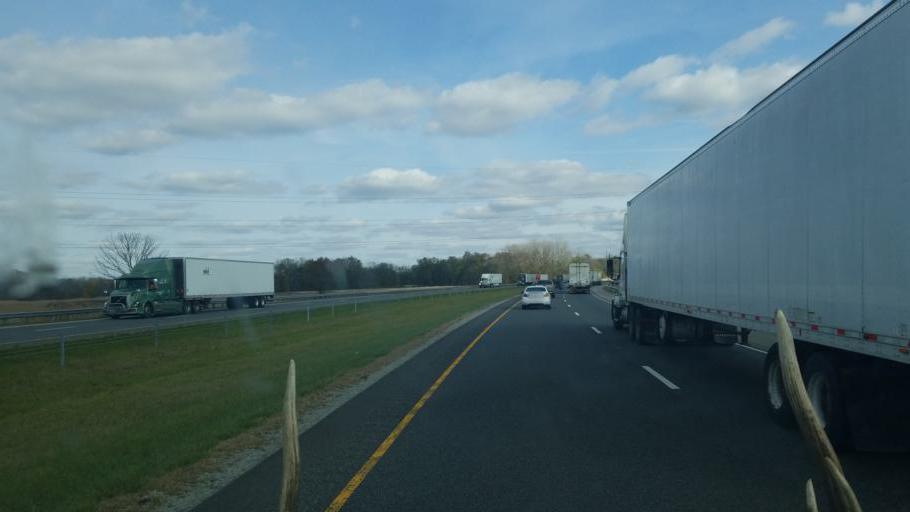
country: US
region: Indiana
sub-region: Henry County
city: Knightstown
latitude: 39.8529
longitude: -85.4827
